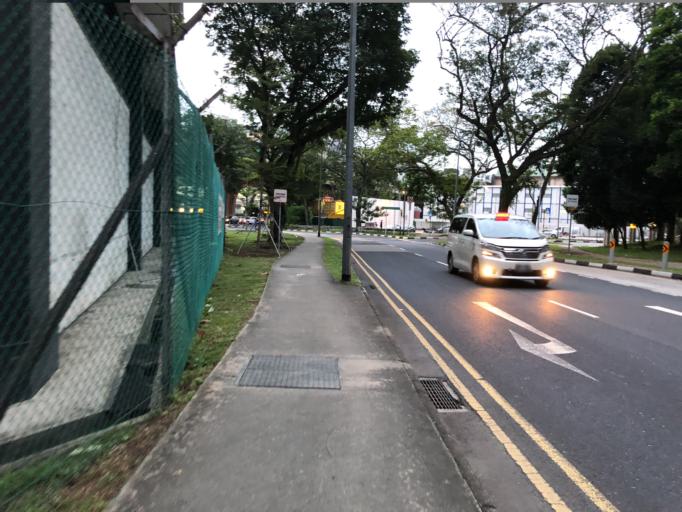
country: SG
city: Singapore
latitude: 1.2735
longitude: 103.8405
